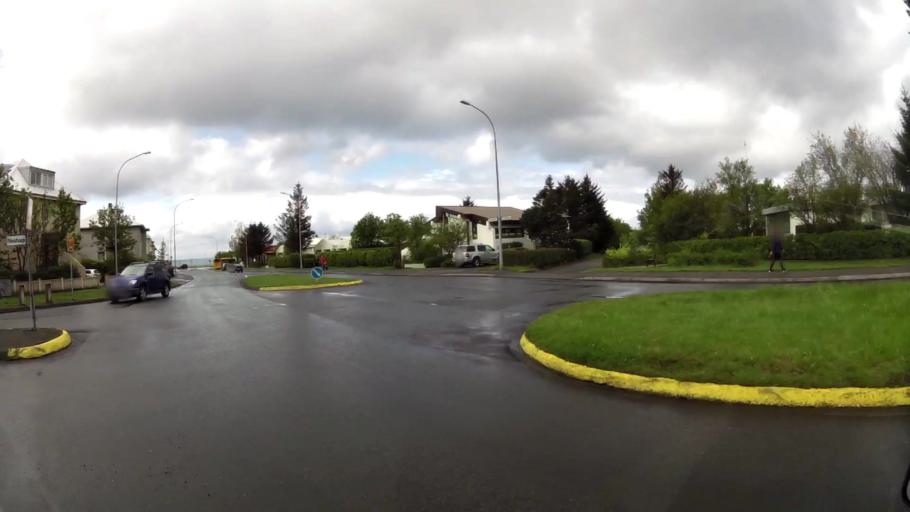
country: IS
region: Capital Region
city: Seltjarnarnes
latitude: 64.1434
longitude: -21.9634
